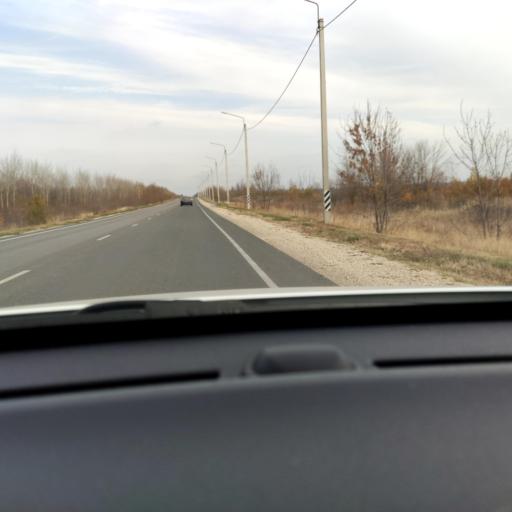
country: RU
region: Voronezj
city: Novaya Usman'
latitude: 51.6704
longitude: 39.4598
